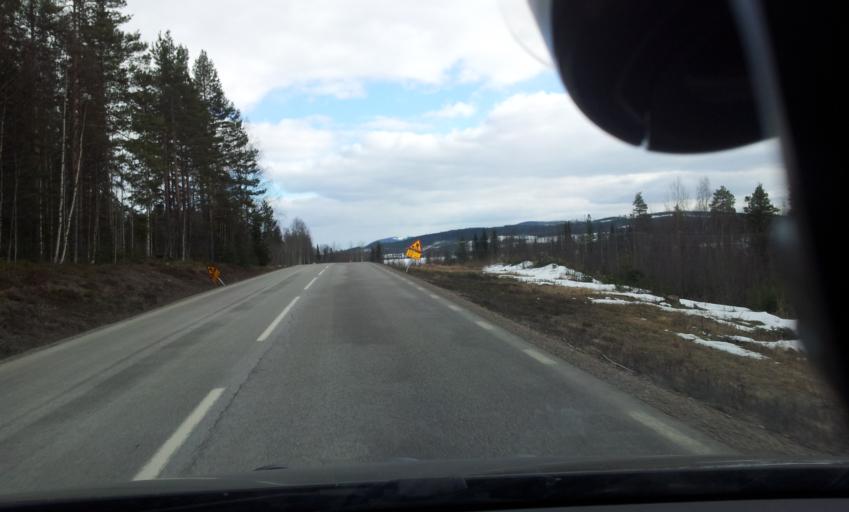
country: SE
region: Gaevleborg
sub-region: Ljusdals Kommun
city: Farila
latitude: 62.1349
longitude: 15.6938
